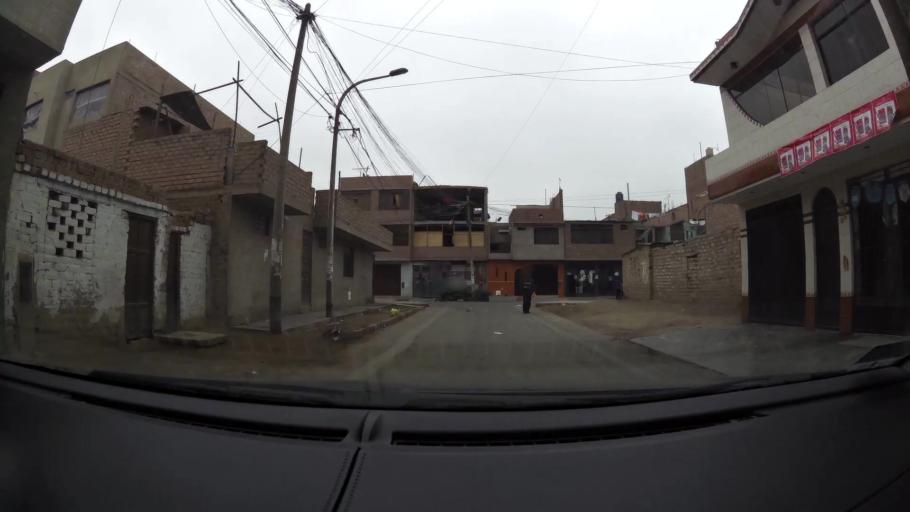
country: PE
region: Lima
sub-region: Lima
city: Independencia
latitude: -11.9553
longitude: -77.0765
